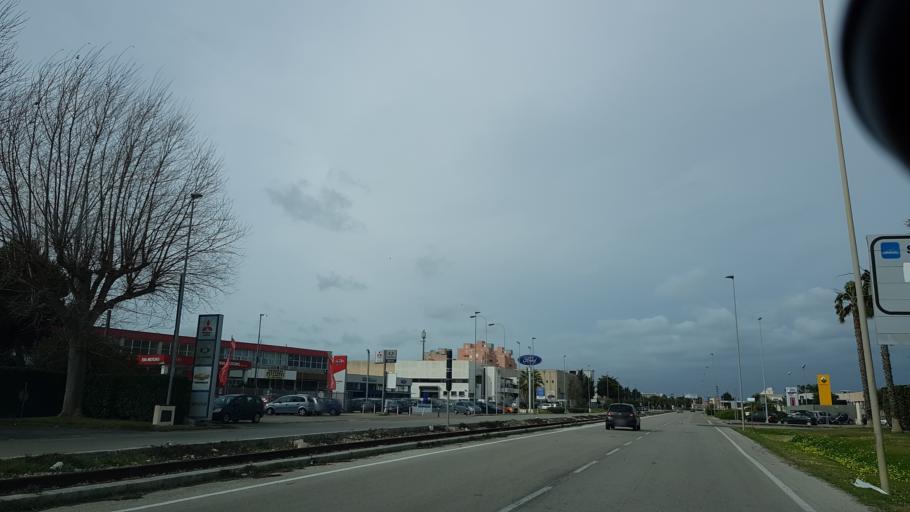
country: IT
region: Apulia
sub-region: Provincia di Brindisi
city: Brindisi
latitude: 40.6305
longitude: 17.9583
